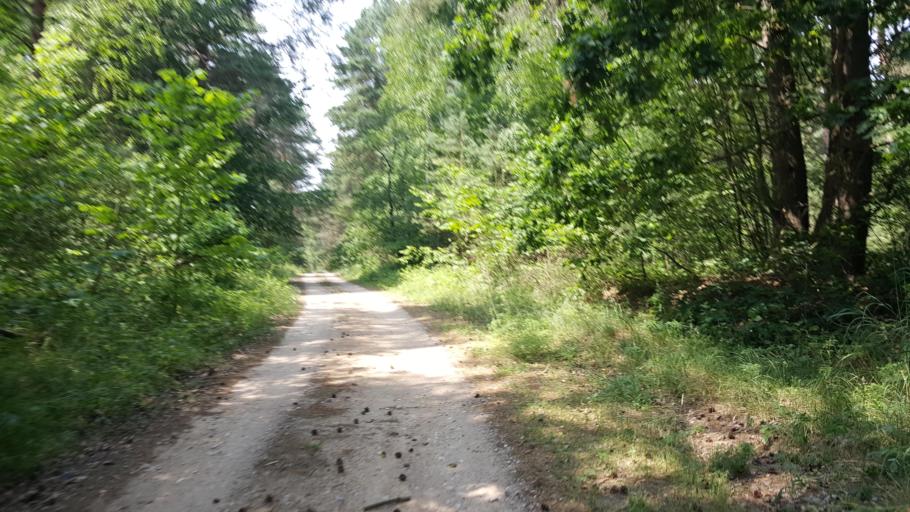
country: BY
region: Brest
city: Kamyanyets
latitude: 52.3679
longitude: 23.7507
